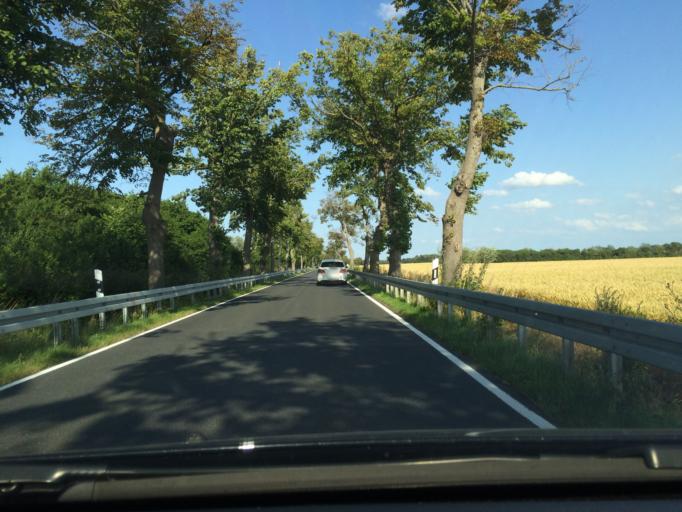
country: DE
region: Mecklenburg-Vorpommern
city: Velgast
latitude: 54.3313
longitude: 12.8492
